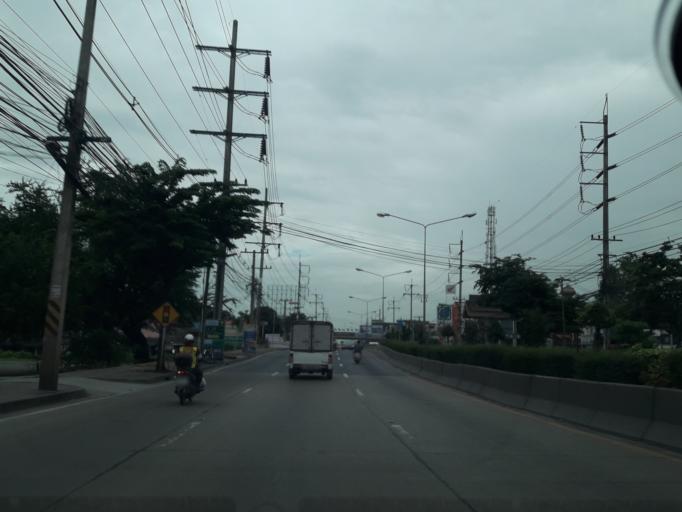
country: TH
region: Pathum Thani
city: Lam Luk Ka
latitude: 13.9350
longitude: 100.7491
